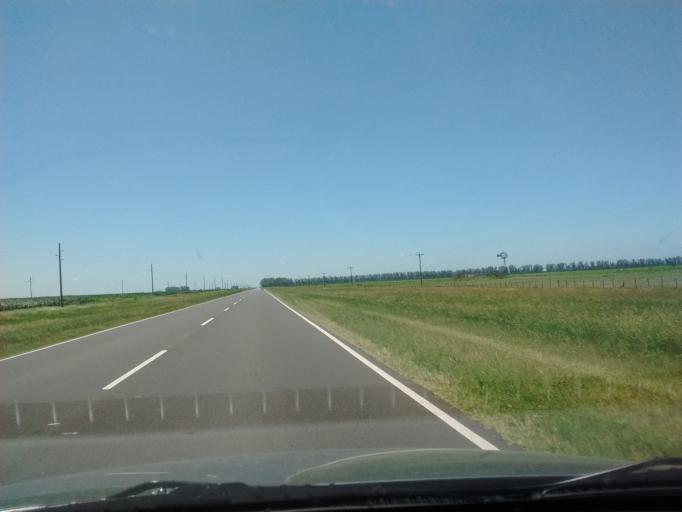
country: AR
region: Entre Rios
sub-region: Departamento de Gualeguay
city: Gualeguay
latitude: -32.9918
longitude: -59.5273
